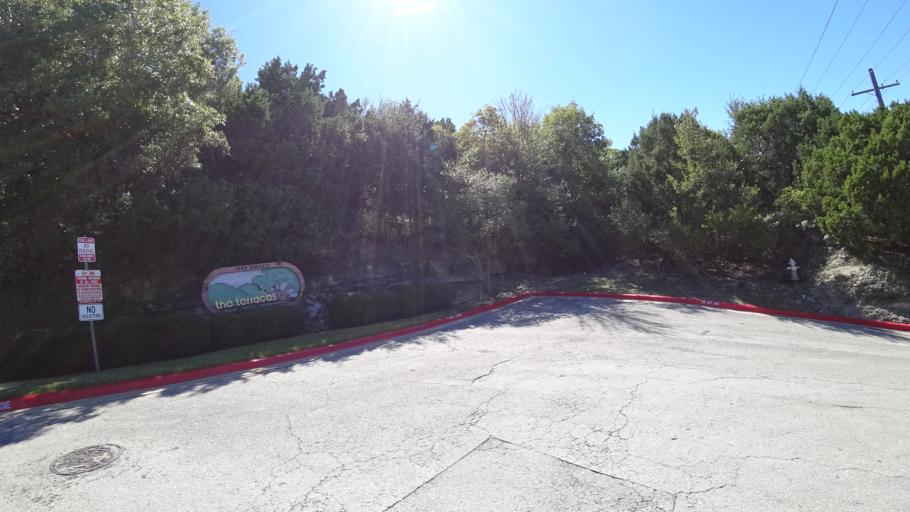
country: US
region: Texas
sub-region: Travis County
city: West Lake Hills
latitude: 30.3417
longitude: -97.7646
